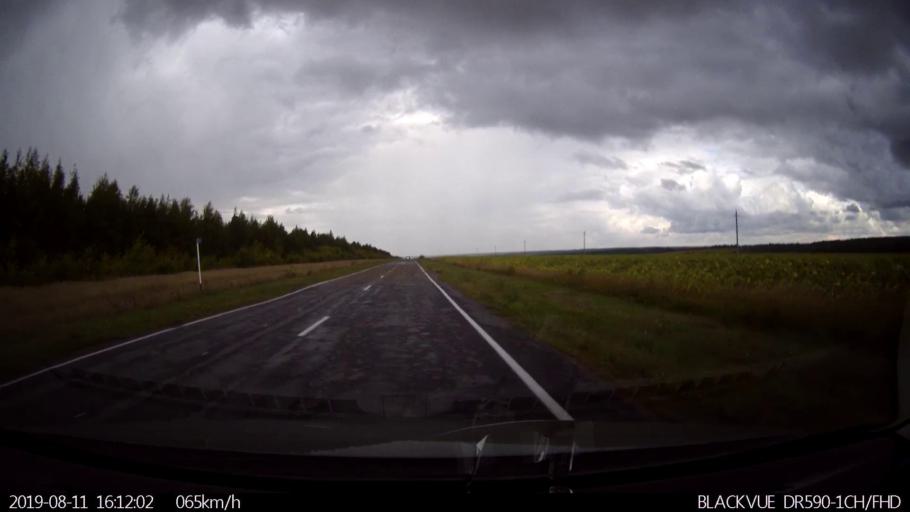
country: RU
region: Ulyanovsk
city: Ignatovka
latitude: 54.0080
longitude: 47.6418
